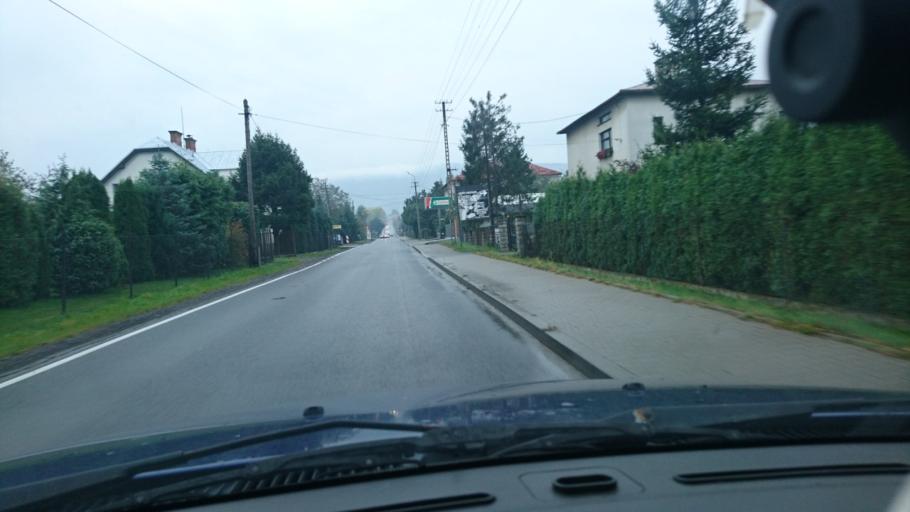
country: PL
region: Silesian Voivodeship
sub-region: Powiat bielski
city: Kozy
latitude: 49.8527
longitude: 19.1413
